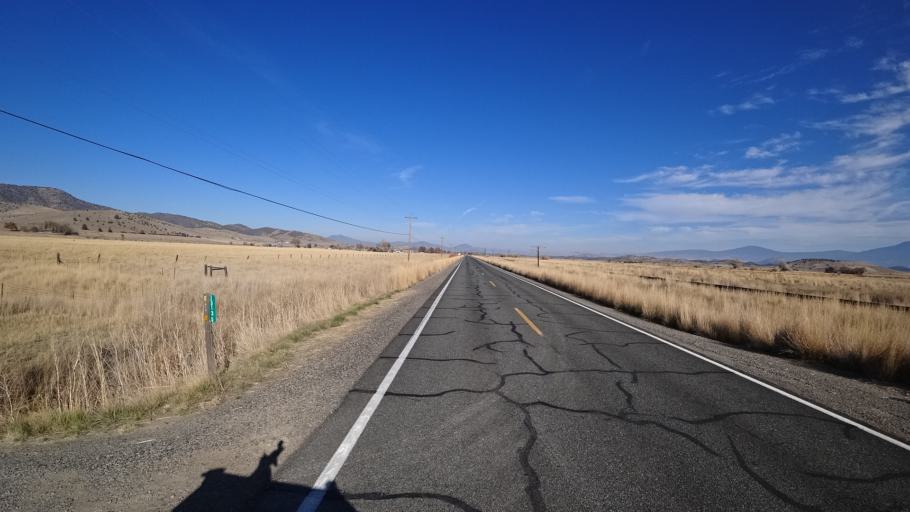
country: US
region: California
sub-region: Siskiyou County
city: Montague
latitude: 41.5962
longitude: -122.5238
